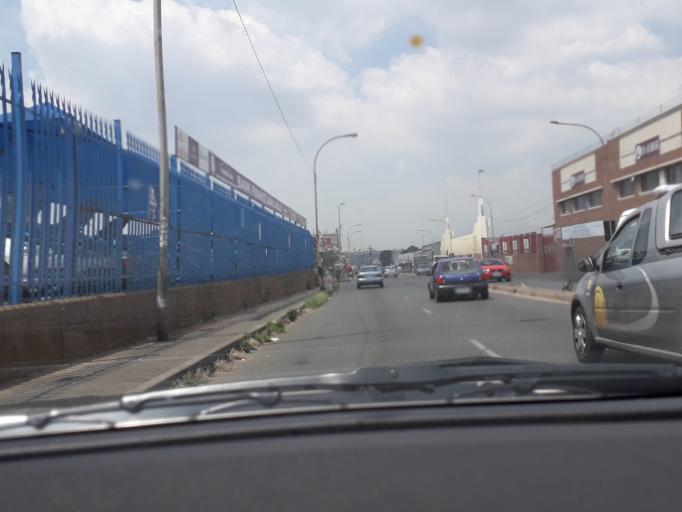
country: ZA
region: Gauteng
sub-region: City of Johannesburg Metropolitan Municipality
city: Johannesburg
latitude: -26.2169
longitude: 28.0437
